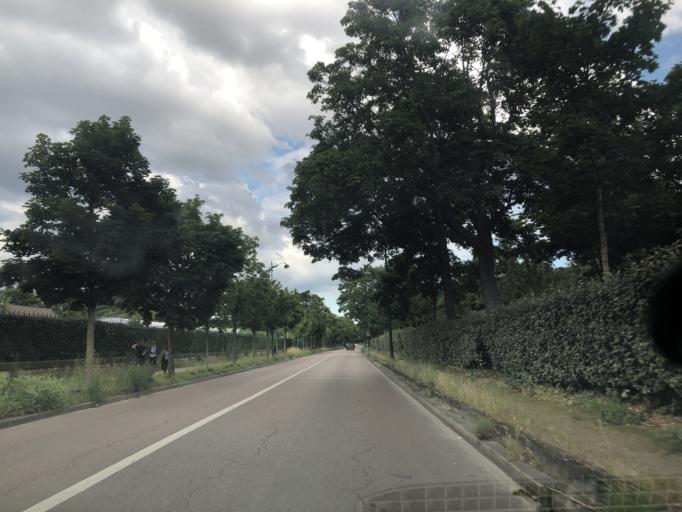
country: FR
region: Ile-de-France
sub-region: Departement du Val-de-Marne
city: Vincennes
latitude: 48.8363
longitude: 2.4419
